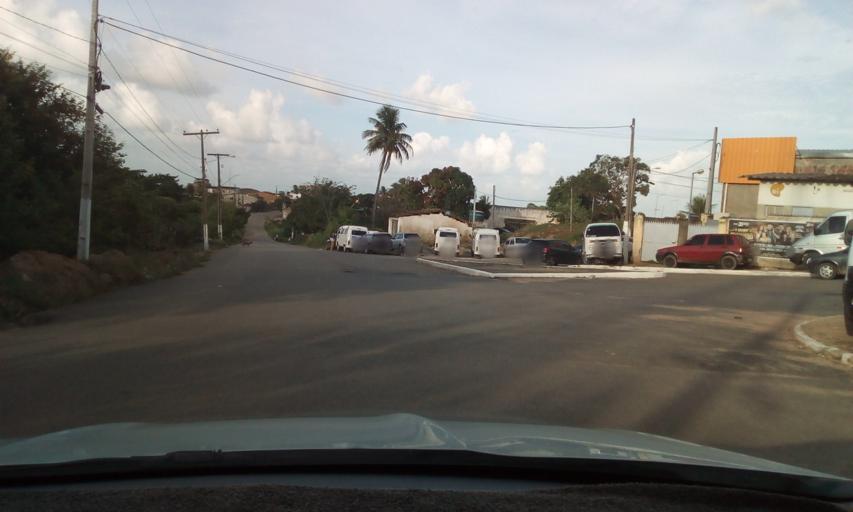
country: BR
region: Pernambuco
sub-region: Gloria Do Goita
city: Gloria do Goita
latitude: -7.9973
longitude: -35.2150
